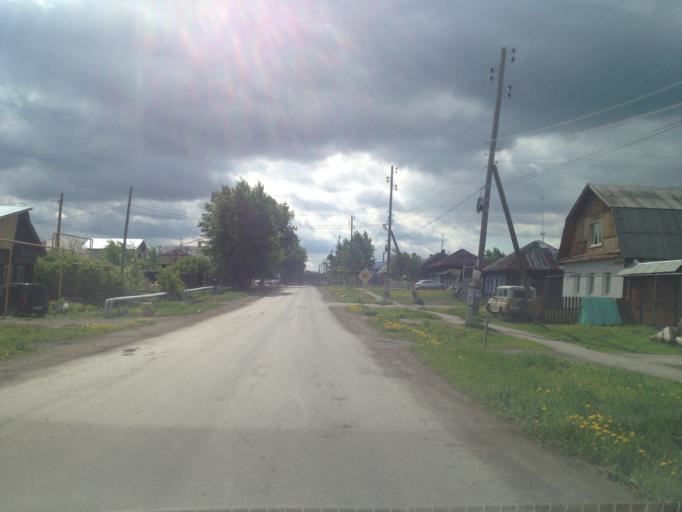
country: RU
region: Sverdlovsk
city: Aramil
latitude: 56.6873
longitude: 60.8519
